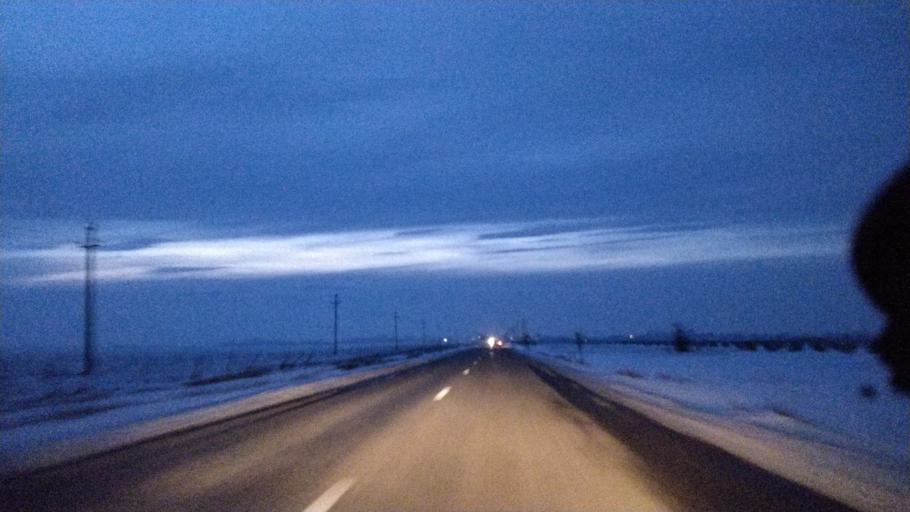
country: RO
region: Vrancea
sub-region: Comuna Rastoaca
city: Rastoaca
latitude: 45.6512
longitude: 27.3120
